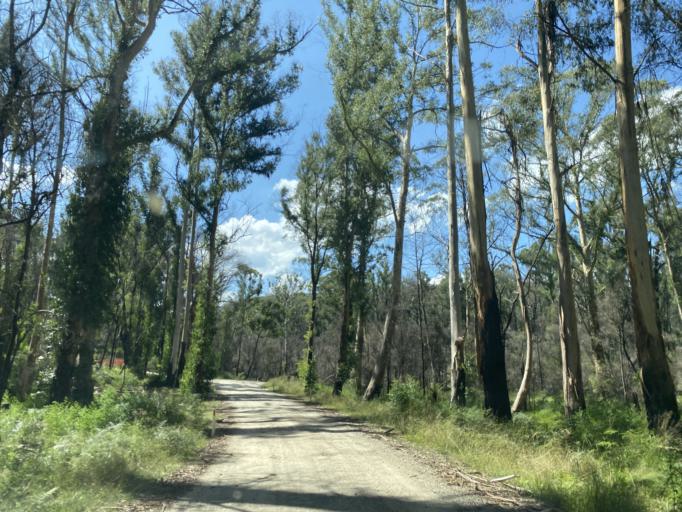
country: AU
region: Victoria
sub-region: Cardinia
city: Gembrook
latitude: -37.9807
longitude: 145.6233
